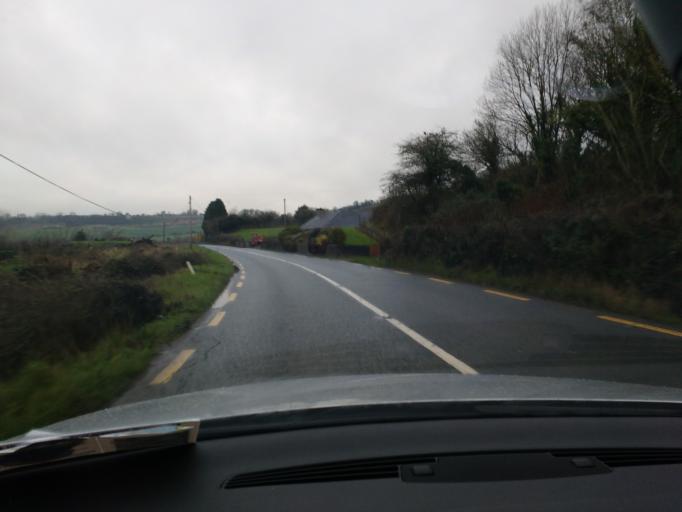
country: IE
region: Munster
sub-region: North Tipperary
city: Nenagh
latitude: 52.8090
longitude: -8.0563
